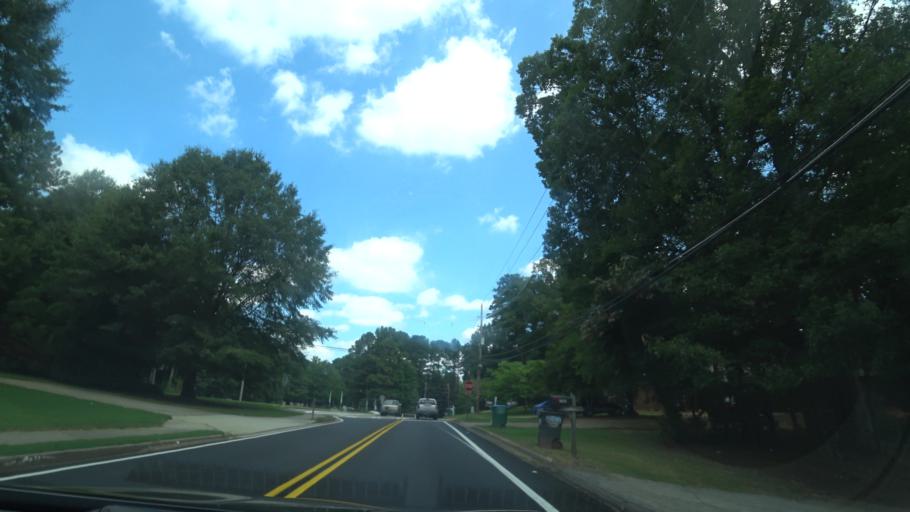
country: US
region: Georgia
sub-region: Gwinnett County
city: Norcross
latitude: 33.9128
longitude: -84.1880
